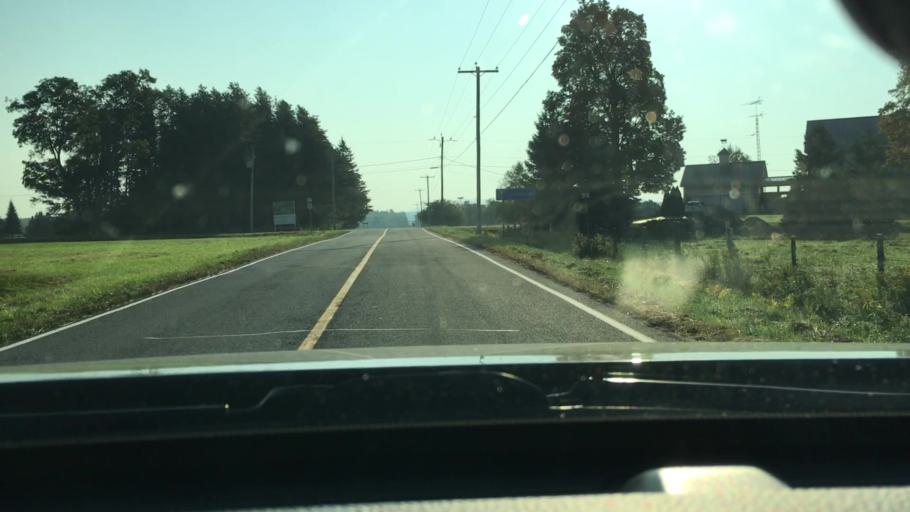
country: CA
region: Quebec
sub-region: Monteregie
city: Waterloo
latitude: 45.3556
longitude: -72.4913
